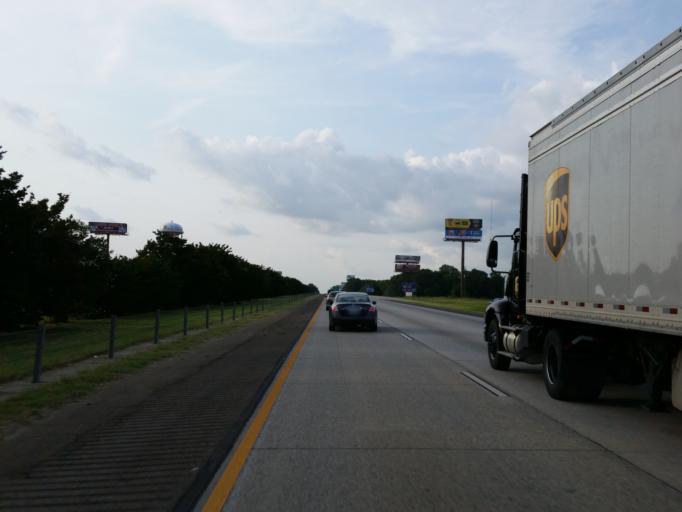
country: US
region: Georgia
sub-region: Peach County
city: Byron
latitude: 32.5902
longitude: -83.7428
